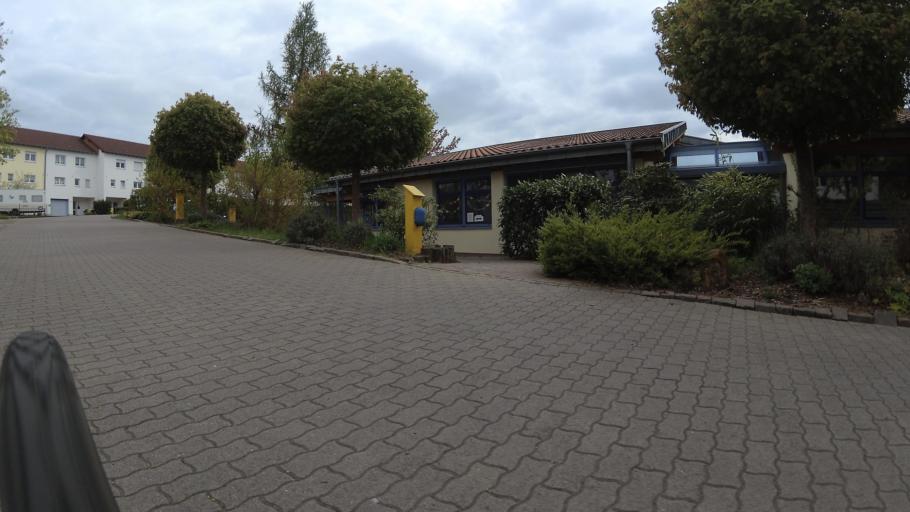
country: DE
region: Rheinland-Pfalz
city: Zweibrucken
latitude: 49.2371
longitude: 7.3694
